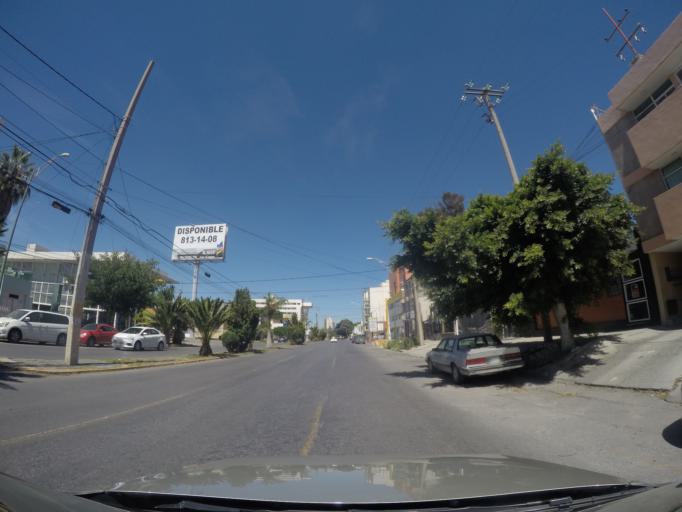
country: MX
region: San Luis Potosi
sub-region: San Luis Potosi
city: San Luis Potosi
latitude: 22.1497
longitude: -100.9984
